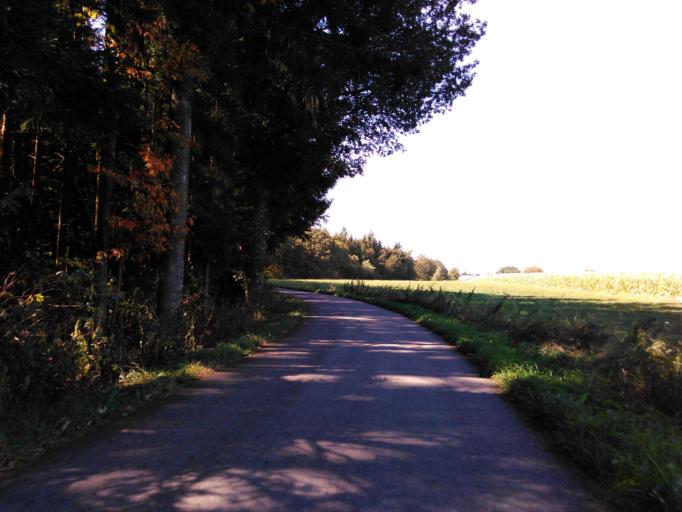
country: LU
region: Diekirch
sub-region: Canton de Redange
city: Rambrouch
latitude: 49.8377
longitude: 5.8222
